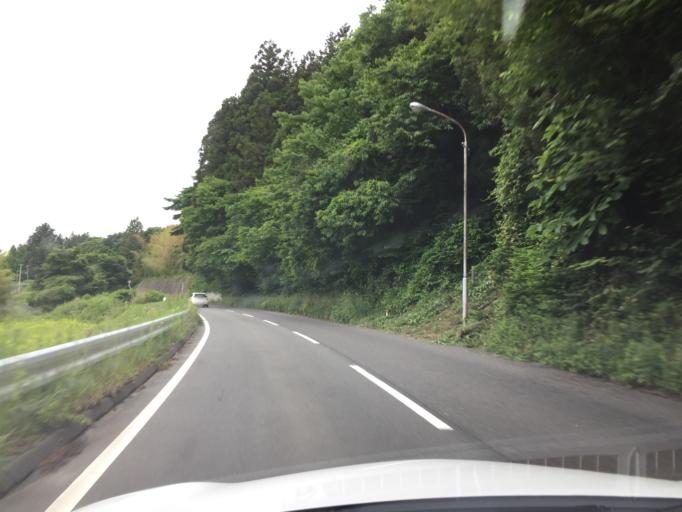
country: JP
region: Fukushima
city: Funehikimachi-funehiki
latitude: 37.3288
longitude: 140.6760
